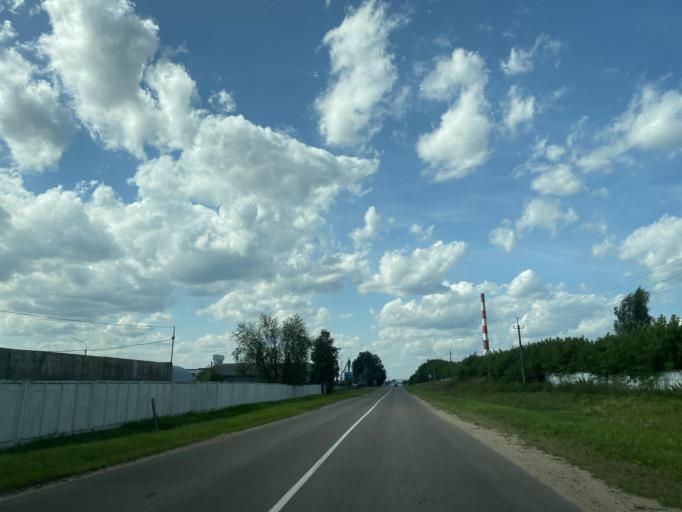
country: BY
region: Minsk
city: Horad Zhodzina
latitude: 54.0863
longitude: 28.3616
